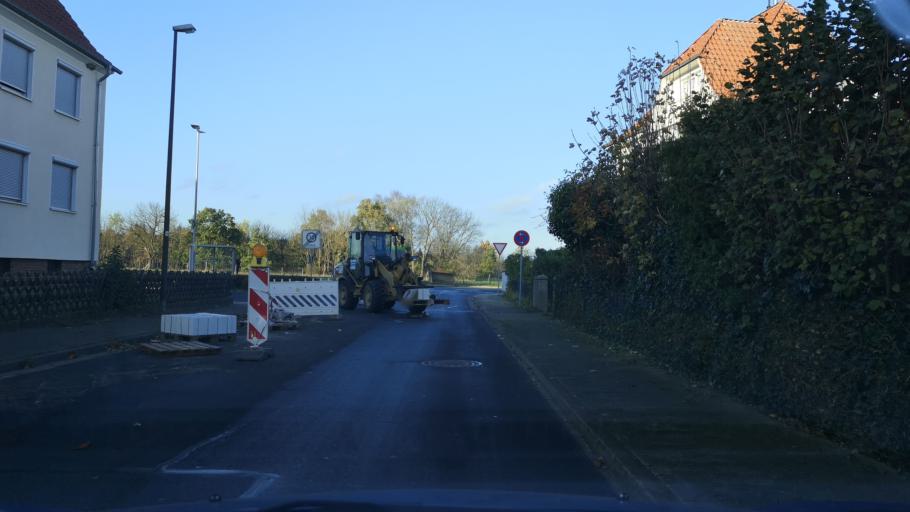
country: DE
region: Lower Saxony
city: Langenhagen
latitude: 52.4528
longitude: 9.7652
